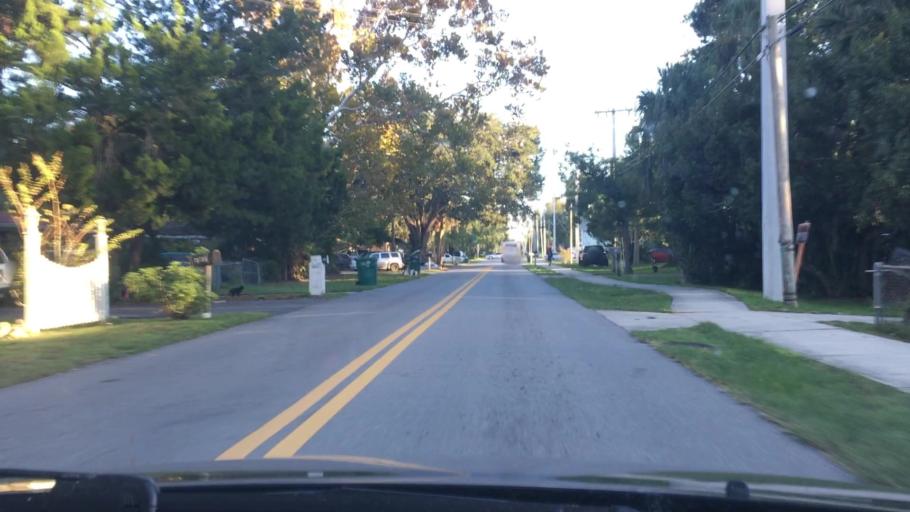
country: US
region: Florida
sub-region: Volusia County
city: Holly Hill
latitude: 29.2338
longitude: -81.0455
